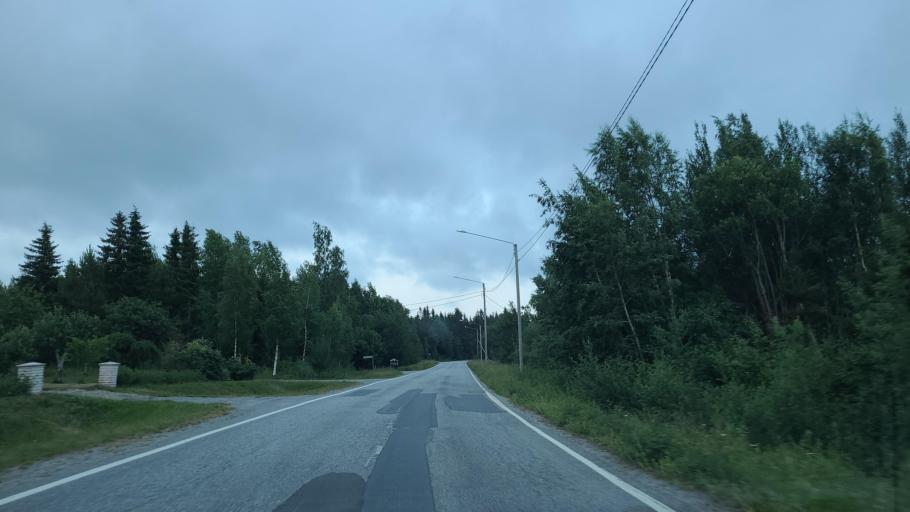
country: FI
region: Ostrobothnia
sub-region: Vaasa
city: Replot
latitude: 63.2810
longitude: 21.1299
